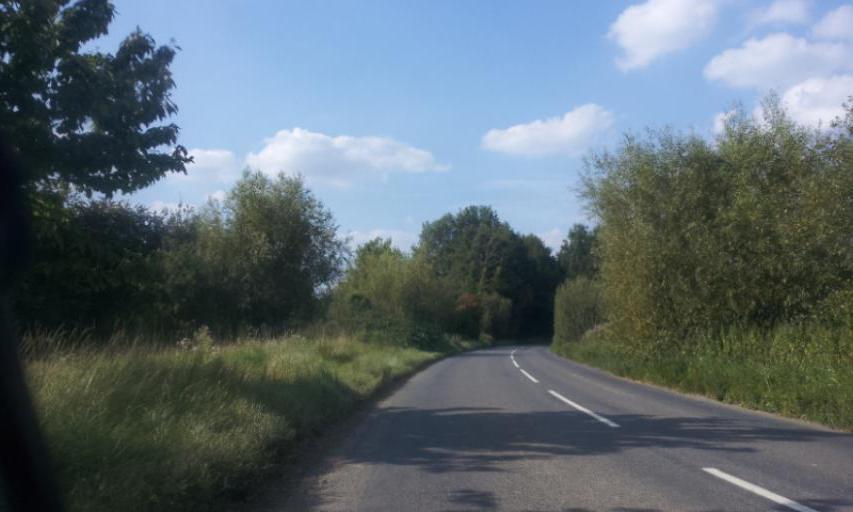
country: GB
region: England
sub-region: Kent
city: Yalding
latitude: 51.1971
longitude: 0.4498
